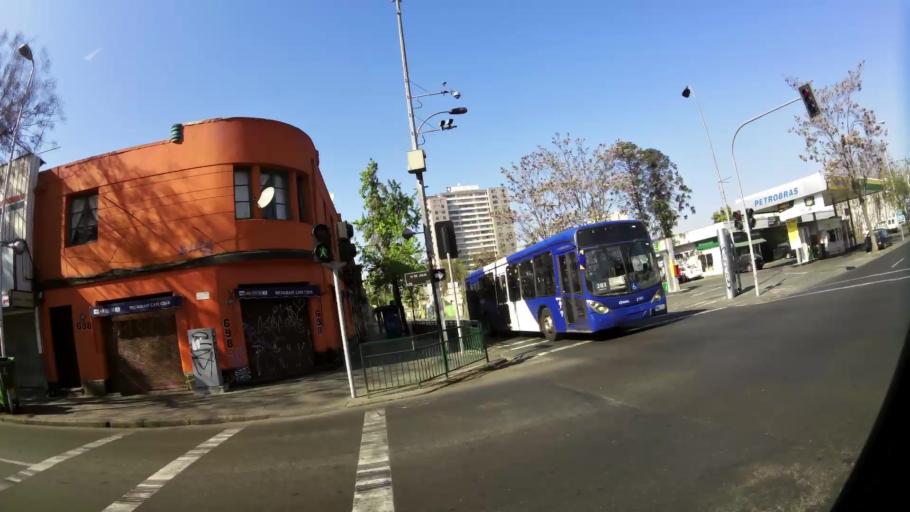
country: CL
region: Santiago Metropolitan
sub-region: Provincia de Santiago
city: Santiago
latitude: -33.4533
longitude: -70.6440
